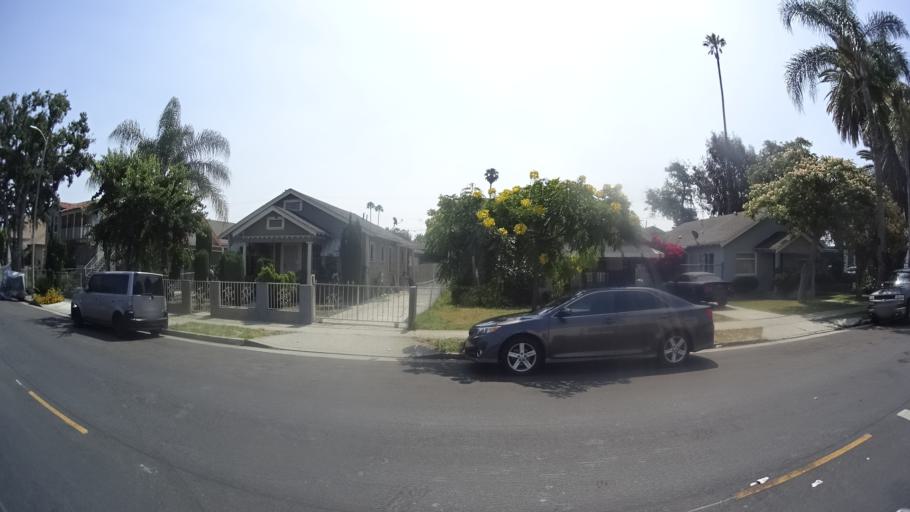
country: US
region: California
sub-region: Los Angeles County
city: View Park-Windsor Hills
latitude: 34.0215
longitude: -118.3248
